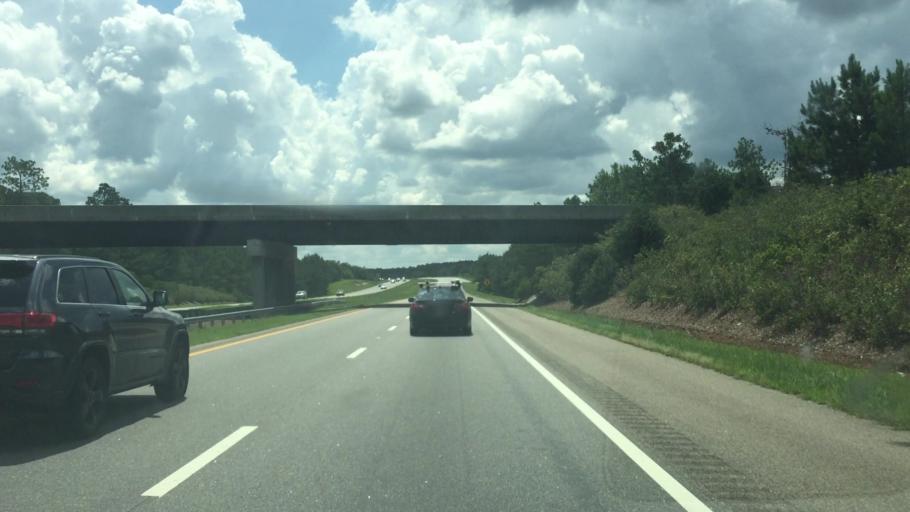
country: US
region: North Carolina
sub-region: Richmond County
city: Hamlet
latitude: 34.8588
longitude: -79.7436
